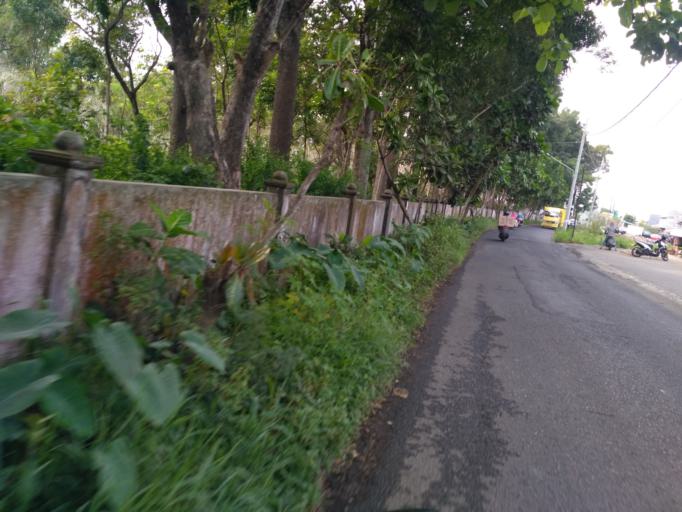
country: ID
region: East Java
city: Malang
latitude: -7.9253
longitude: 112.6047
